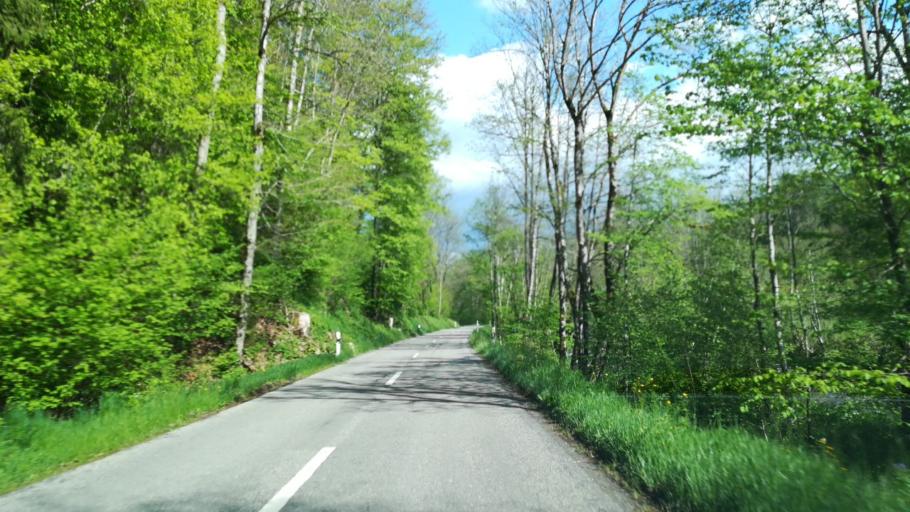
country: DE
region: Baden-Wuerttemberg
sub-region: Freiburg Region
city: Blumberg
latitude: 47.8434
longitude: 8.4696
